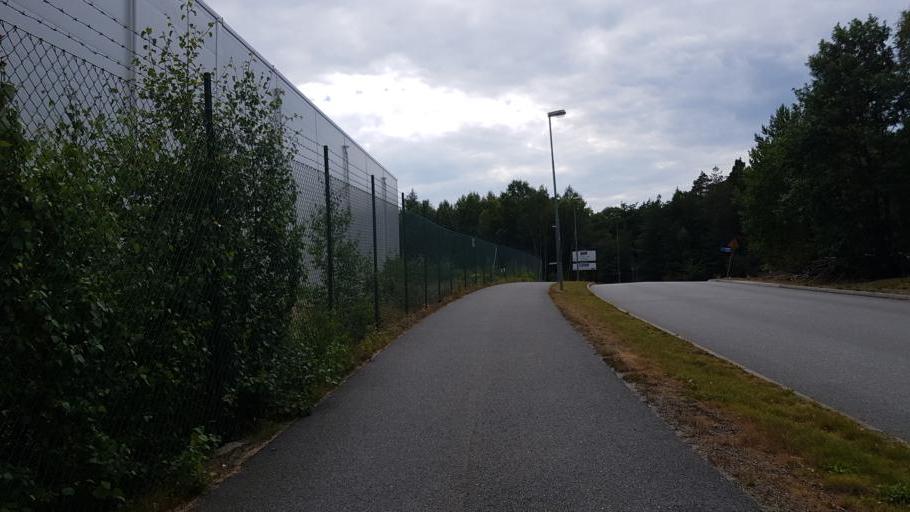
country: SE
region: Vaestra Goetaland
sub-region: Harryda Kommun
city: Molnlycke
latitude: 57.6756
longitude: 12.0859
